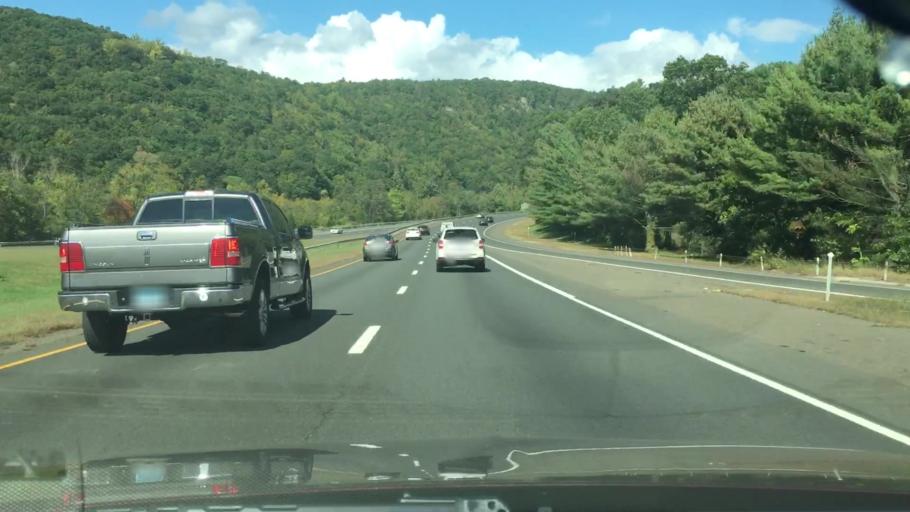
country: US
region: Connecticut
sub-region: New Haven County
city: Naugatuck
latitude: 41.4459
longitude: -73.0670
